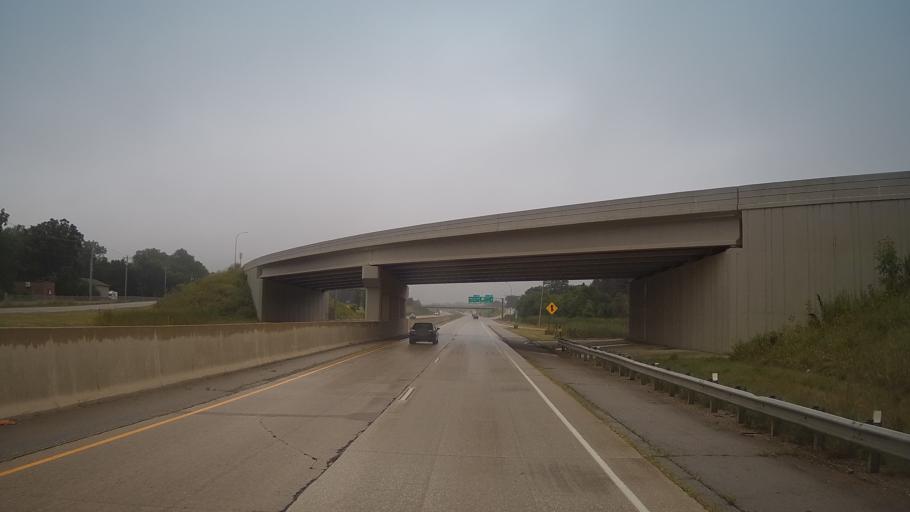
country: US
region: Minnesota
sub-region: Mower County
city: Austin
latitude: 43.6742
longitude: -92.9470
